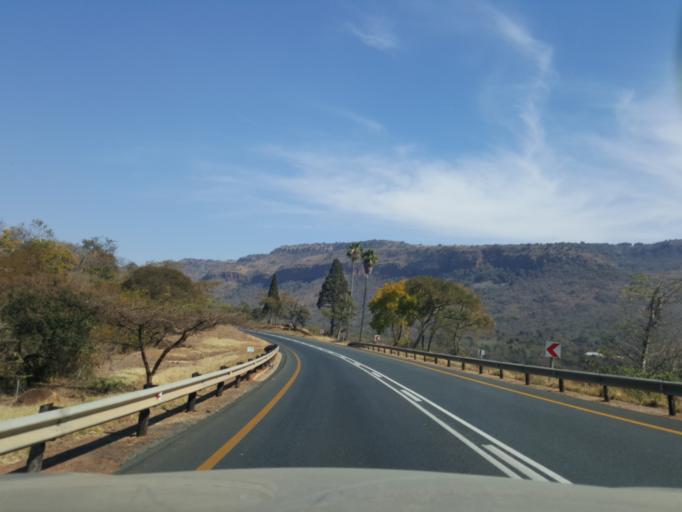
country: ZA
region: Mpumalanga
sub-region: Ehlanzeni District
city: Lydenburg
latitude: -25.3849
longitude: 30.5297
